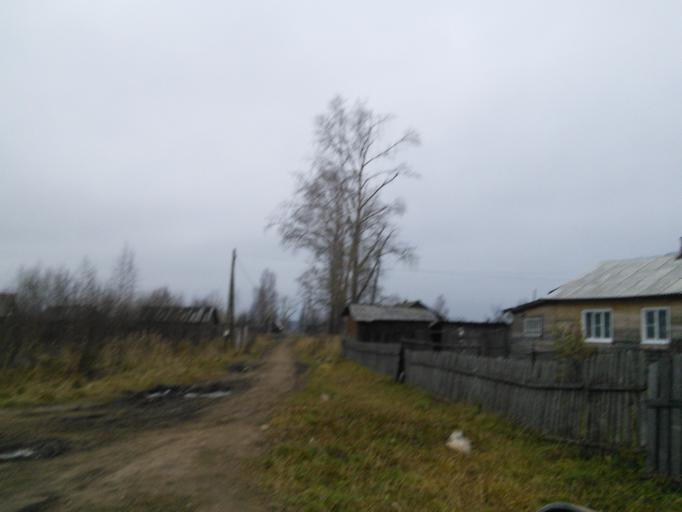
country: RU
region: Vologda
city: Kharovsk
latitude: 59.8081
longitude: 40.1755
